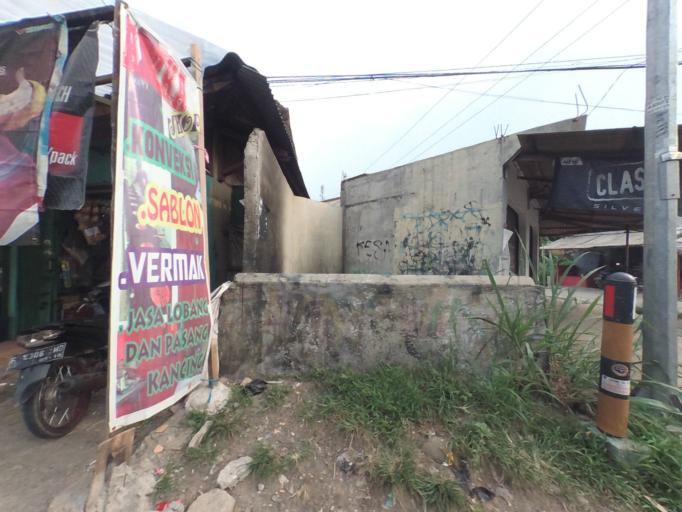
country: ID
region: West Java
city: Ciampea
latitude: -6.5648
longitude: 106.6757
